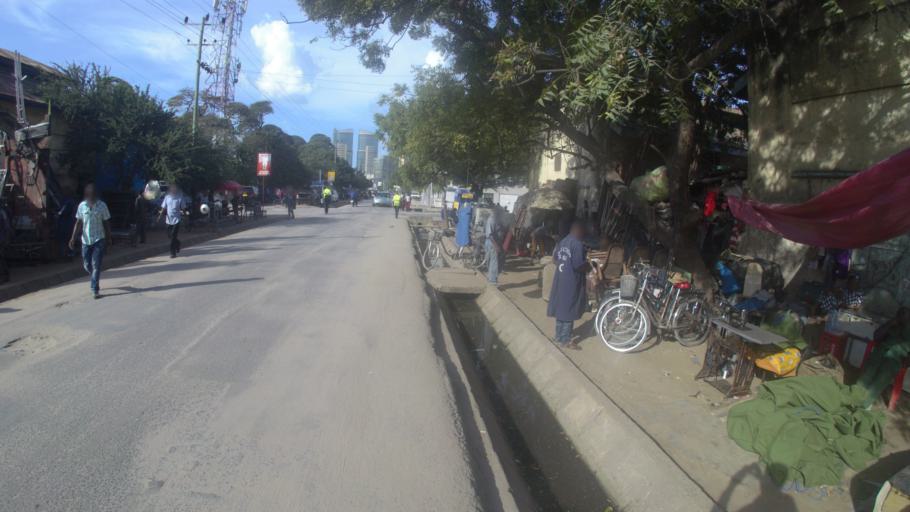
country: TZ
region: Dar es Salaam
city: Dar es Salaam
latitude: -6.8252
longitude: 39.2784
